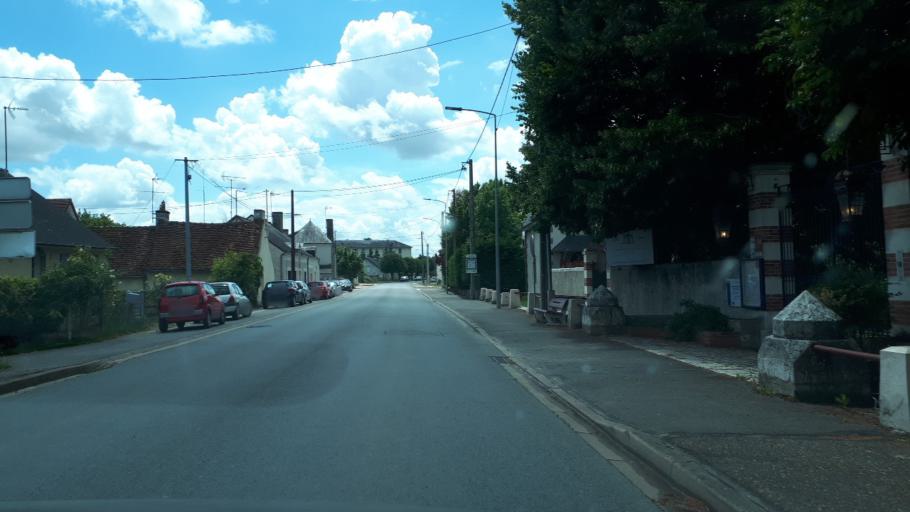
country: FR
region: Centre
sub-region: Departement du Loir-et-Cher
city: Contres
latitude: 47.4160
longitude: 1.4278
